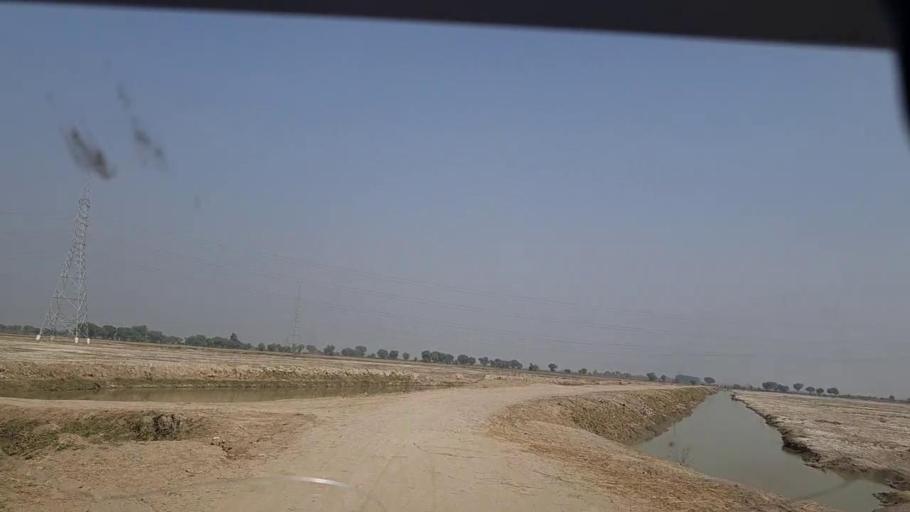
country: PK
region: Sindh
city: Shikarpur
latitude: 28.0346
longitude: 68.6312
